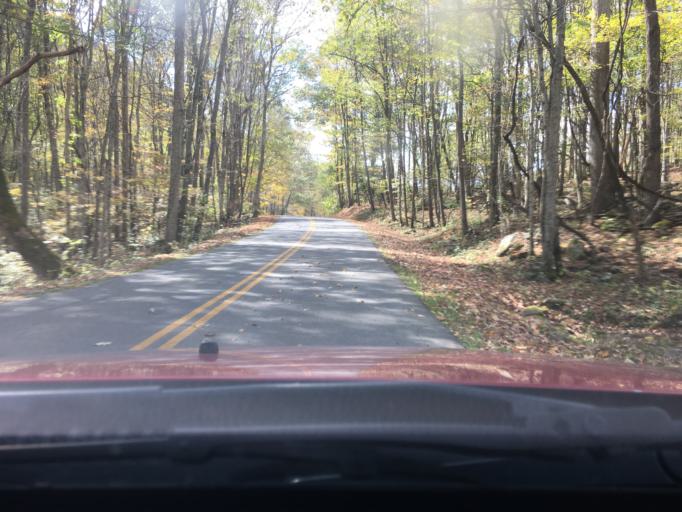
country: US
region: Virginia
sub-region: Giles County
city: Pembroke
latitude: 37.3501
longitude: -80.6018
